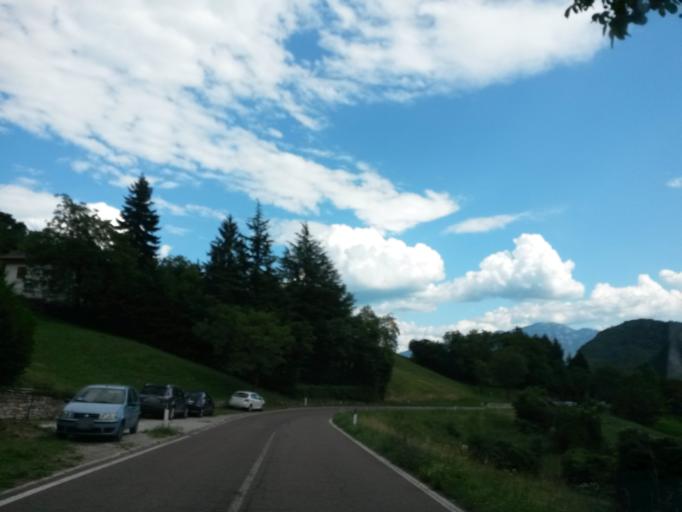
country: IT
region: Trentino-Alto Adige
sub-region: Provincia di Trento
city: Tenno
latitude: 45.9330
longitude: 10.8153
